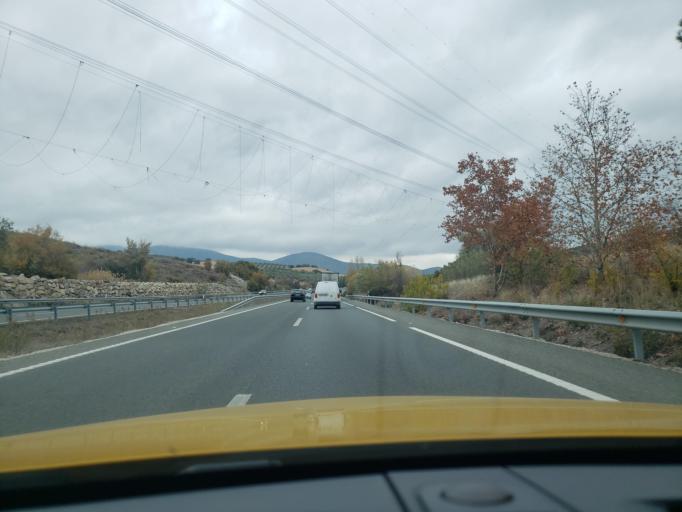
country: ES
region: Andalusia
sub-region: Provincia de Granada
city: Deifontes
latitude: 37.3549
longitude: -3.6132
